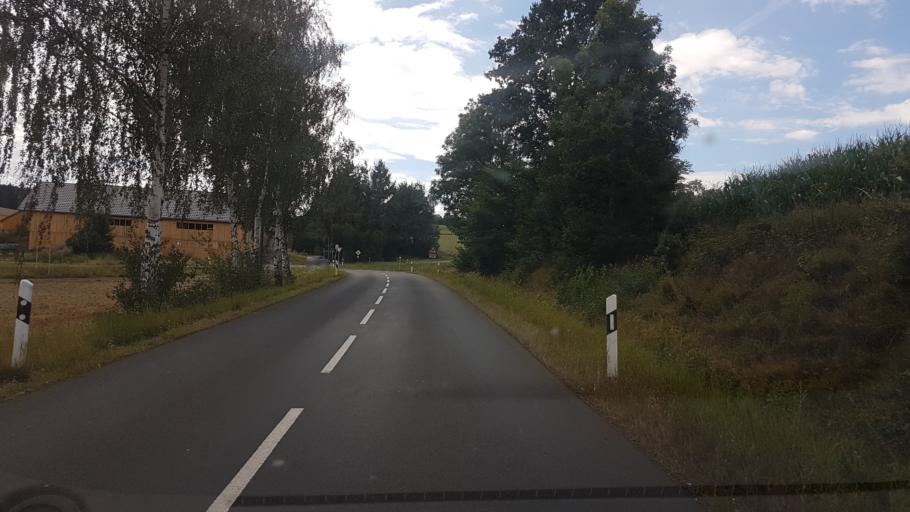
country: DE
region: Bavaria
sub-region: Upper Palatinate
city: Waldsassen
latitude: 50.0337
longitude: 12.3018
